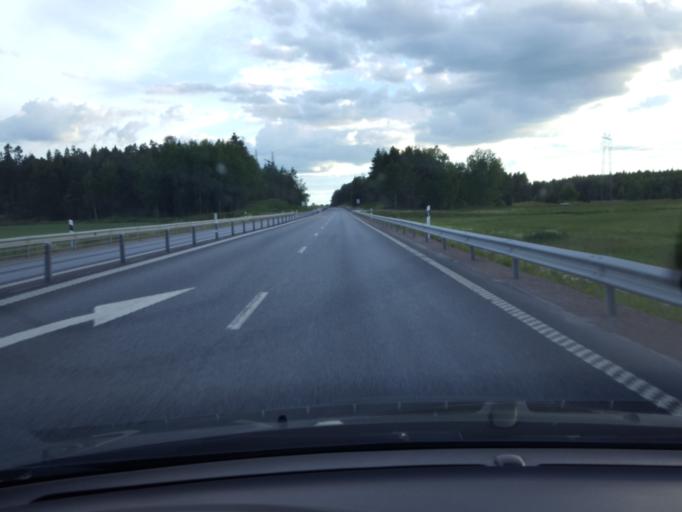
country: SE
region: Uppsala
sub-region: Osthammars Kommun
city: Osterbybruk
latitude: 60.0298
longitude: 18.0107
